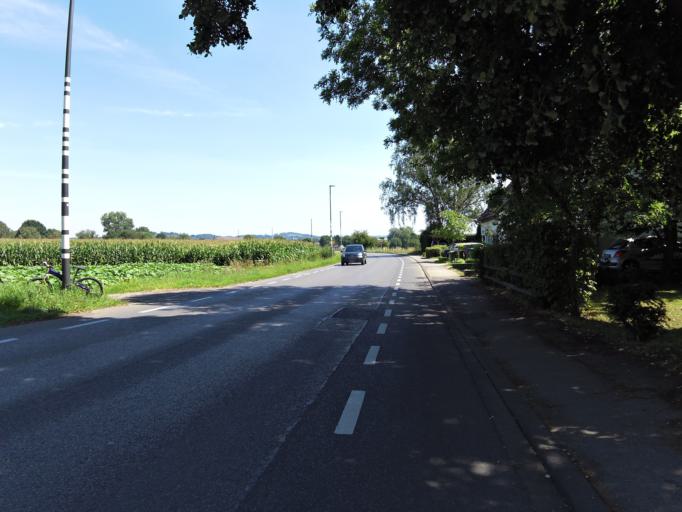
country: DE
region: North Rhine-Westphalia
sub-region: Regierungsbezirk Koln
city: Aachen
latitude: 50.7999
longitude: 6.0772
